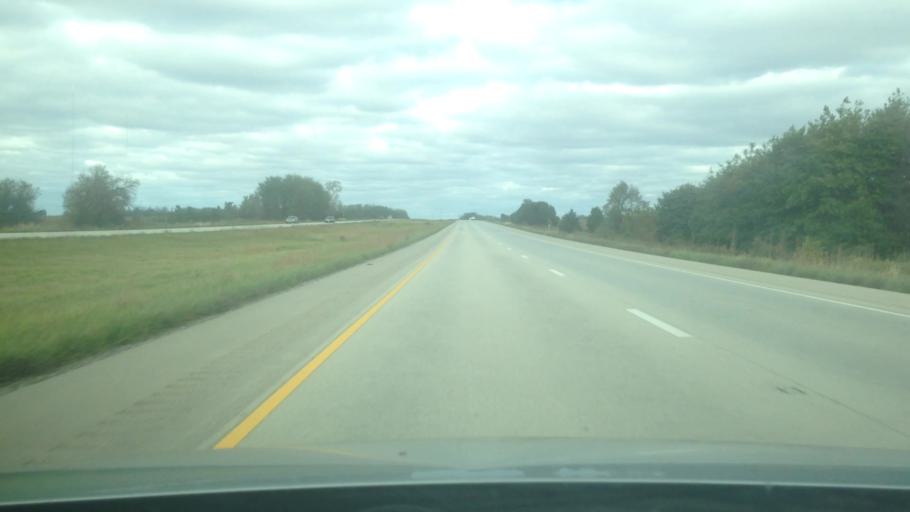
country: US
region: Illinois
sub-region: Macon County
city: Forsyth
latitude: 39.9232
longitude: -88.8539
